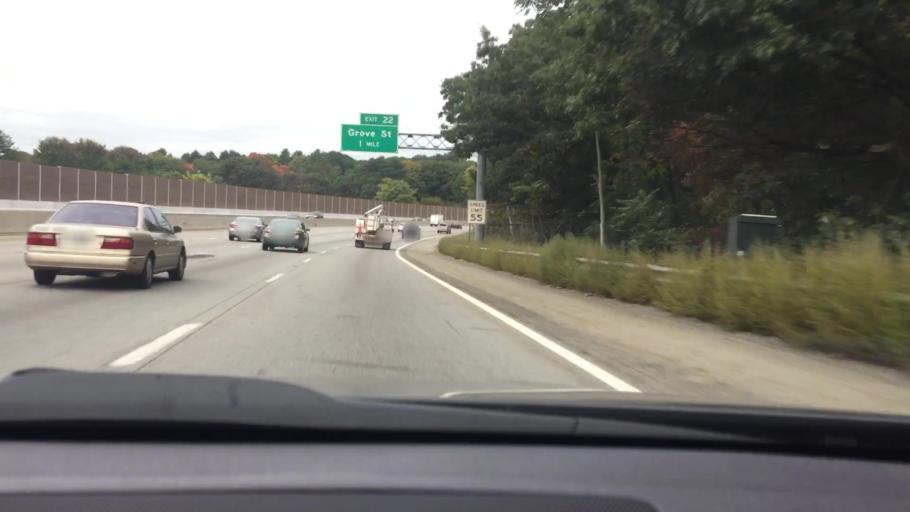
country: US
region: Massachusetts
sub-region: Middlesex County
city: Newton
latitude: 42.3200
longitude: -71.2424
